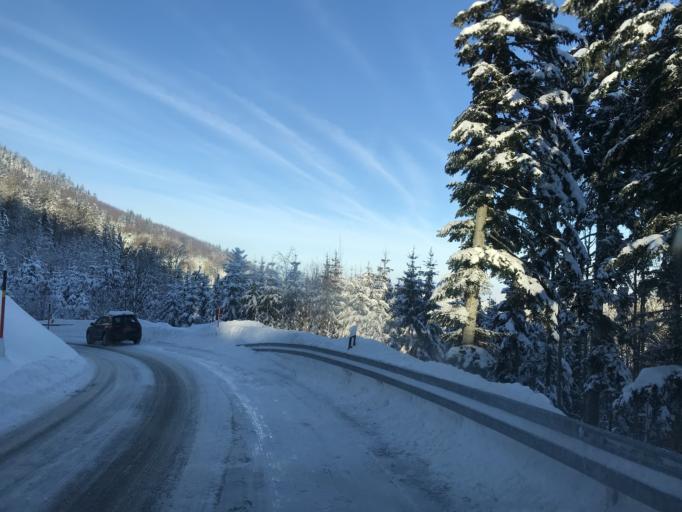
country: DE
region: Baden-Wuerttemberg
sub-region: Freiburg Region
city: Muenstertal/Schwarzwald
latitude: 47.8040
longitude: 7.7894
